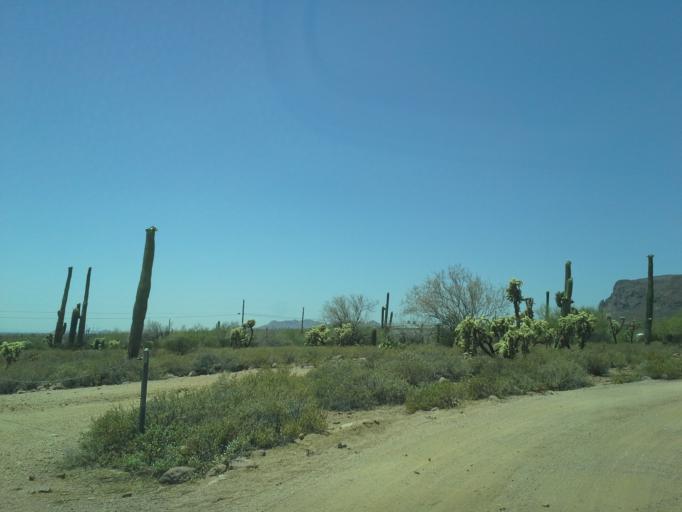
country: US
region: Arizona
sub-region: Pinal County
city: Apache Junction
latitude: 33.3916
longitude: -111.4367
